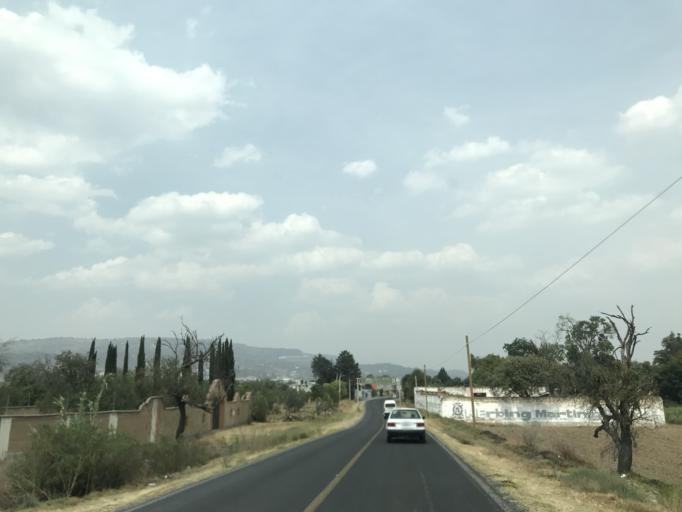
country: MX
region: Tlaxcala
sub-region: Ixtacuixtla de Mariano Matamoros
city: Santa Justina Ecatepec
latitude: 19.3169
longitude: -98.3204
